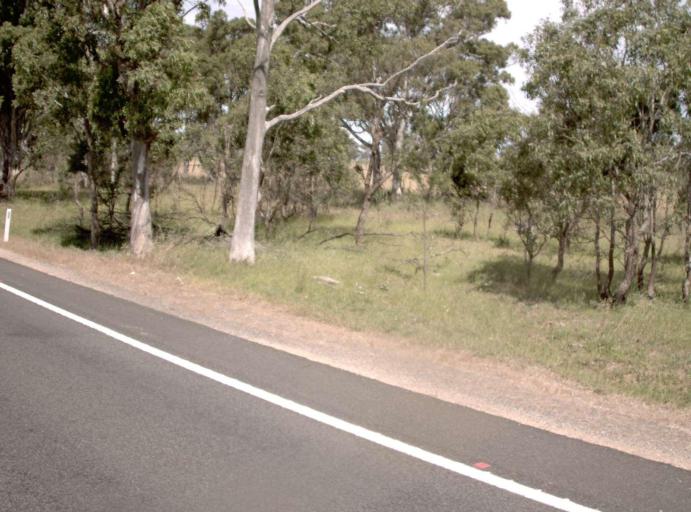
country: AU
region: Victoria
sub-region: East Gippsland
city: Bairnsdale
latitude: -37.8628
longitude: 147.5048
